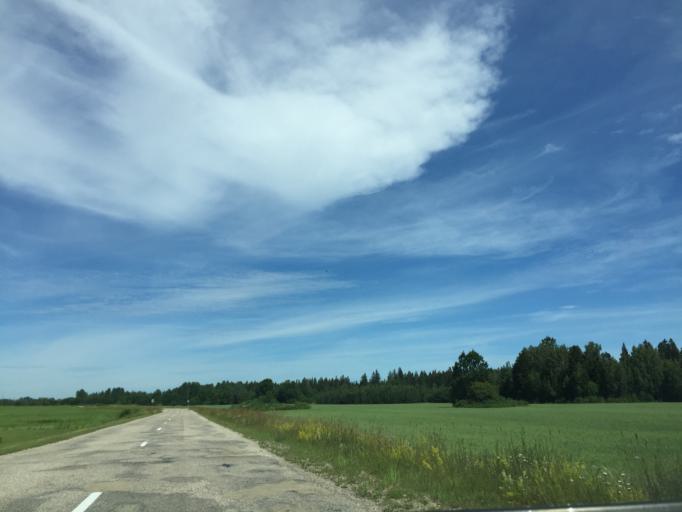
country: LV
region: Dundaga
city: Dundaga
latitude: 57.5395
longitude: 22.3287
